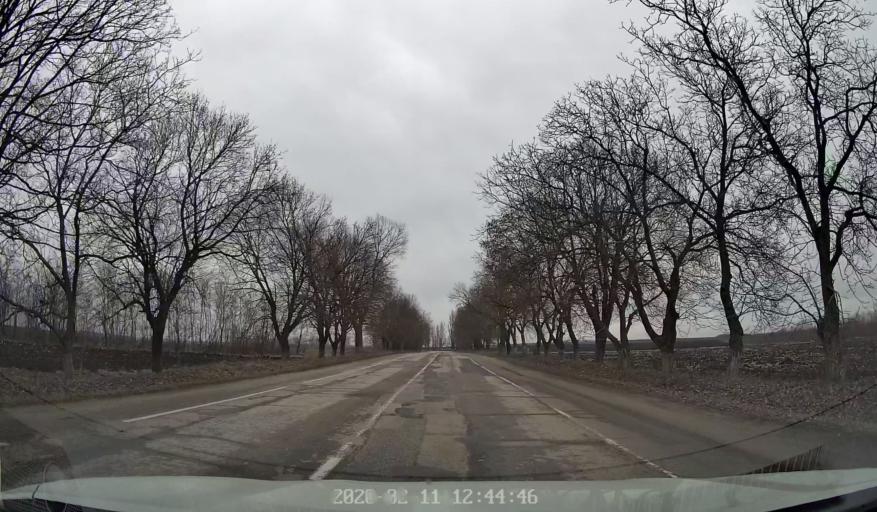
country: MD
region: Raionul Edinet
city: Edinet
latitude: 48.2499
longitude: 27.2006
